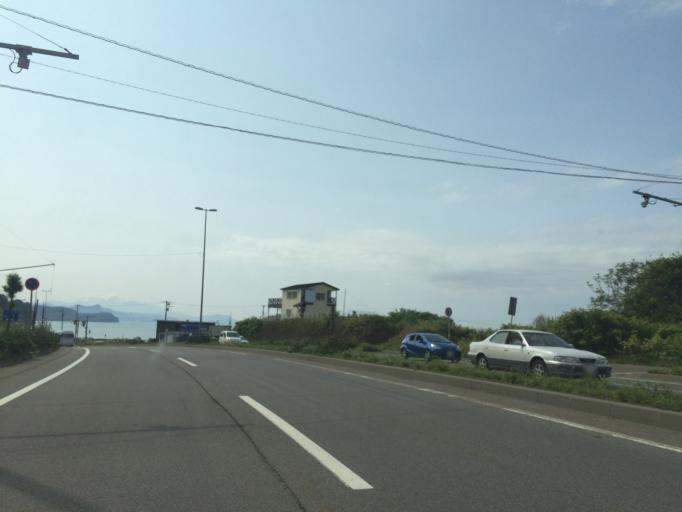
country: JP
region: Hokkaido
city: Otaru
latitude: 43.2106
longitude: 140.9182
